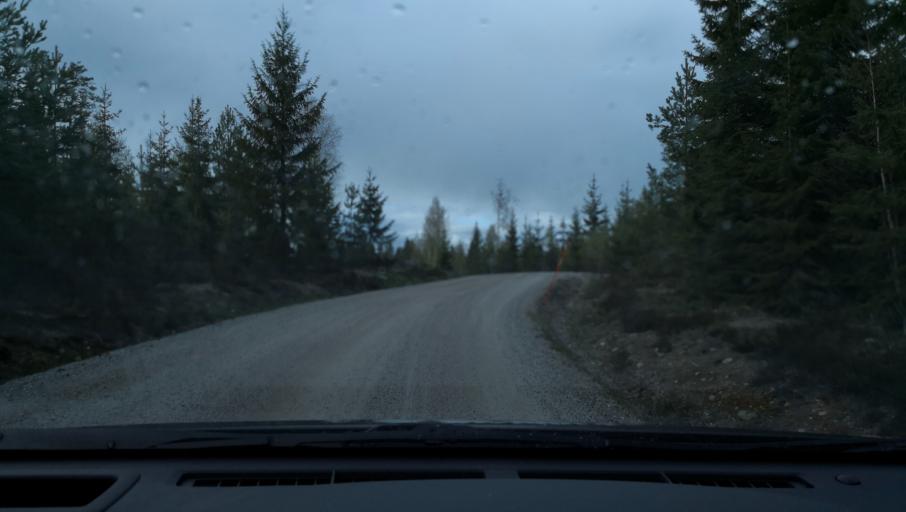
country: SE
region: Dalarna
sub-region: Saters Kommun
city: Saeter
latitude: 60.1736
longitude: 15.7259
